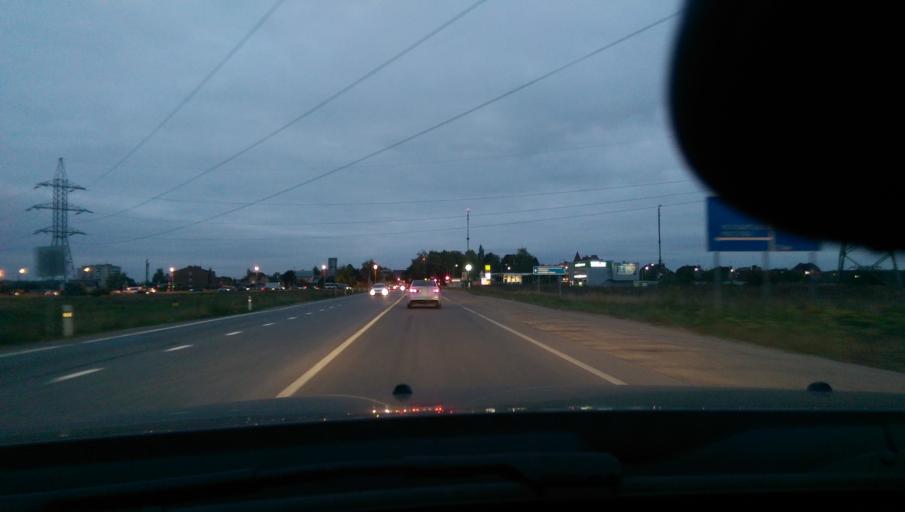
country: RU
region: Moskovskaya
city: Povedniki
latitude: 55.9557
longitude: 37.6507
